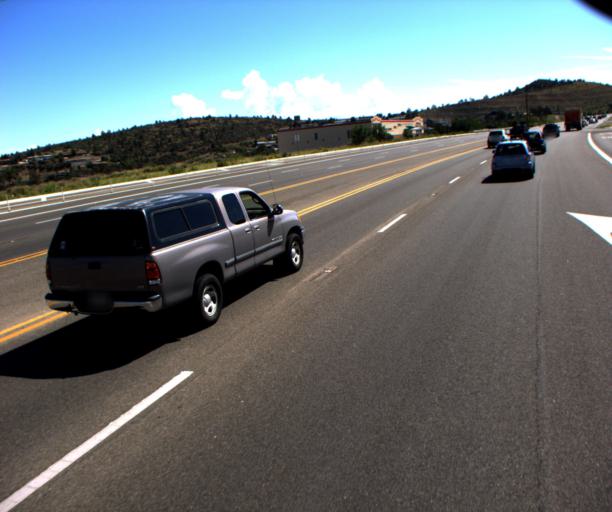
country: US
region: Arizona
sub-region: Yavapai County
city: Prescott
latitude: 34.5521
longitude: -112.4308
